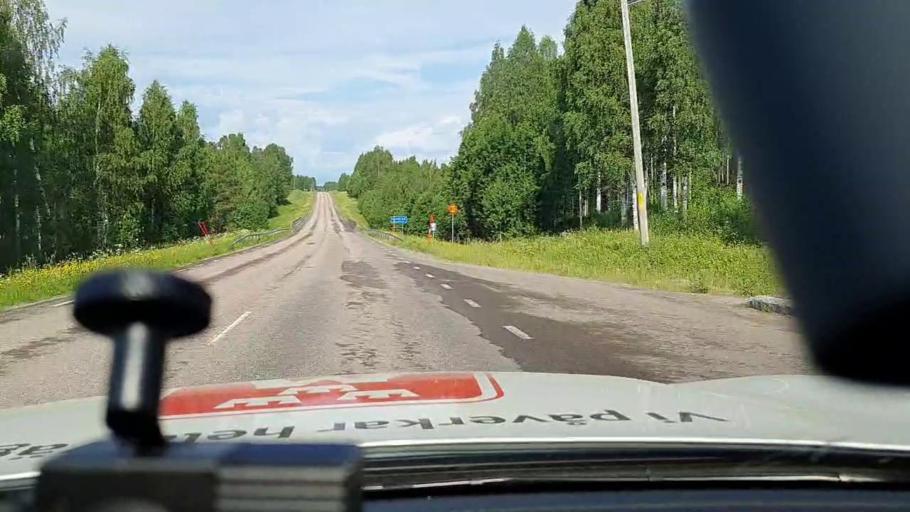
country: SE
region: Norrbotten
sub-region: Alvsbyns Kommun
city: AElvsbyn
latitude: 66.0131
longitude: 21.1701
